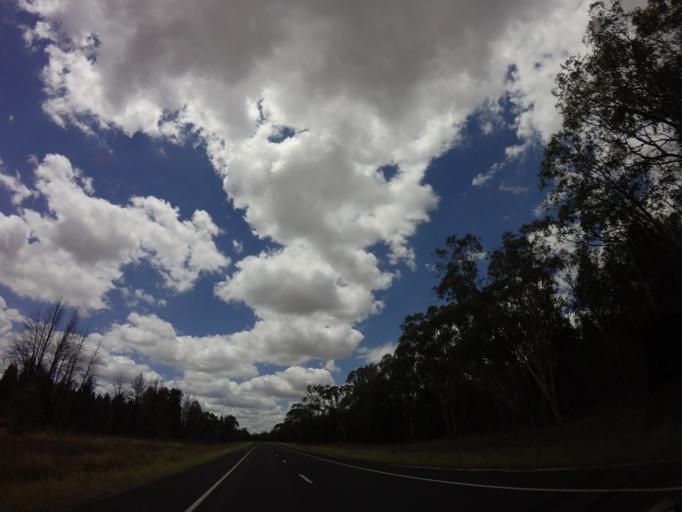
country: AU
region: Queensland
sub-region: Goondiwindi
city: Goondiwindi
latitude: -28.1187
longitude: 150.7104
